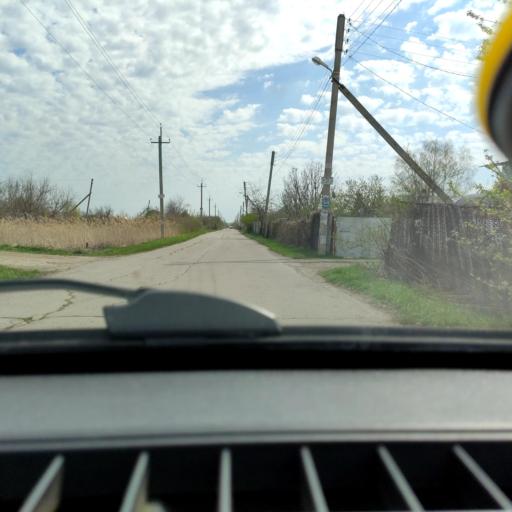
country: RU
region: Samara
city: Tol'yatti
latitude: 53.7013
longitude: 49.4293
